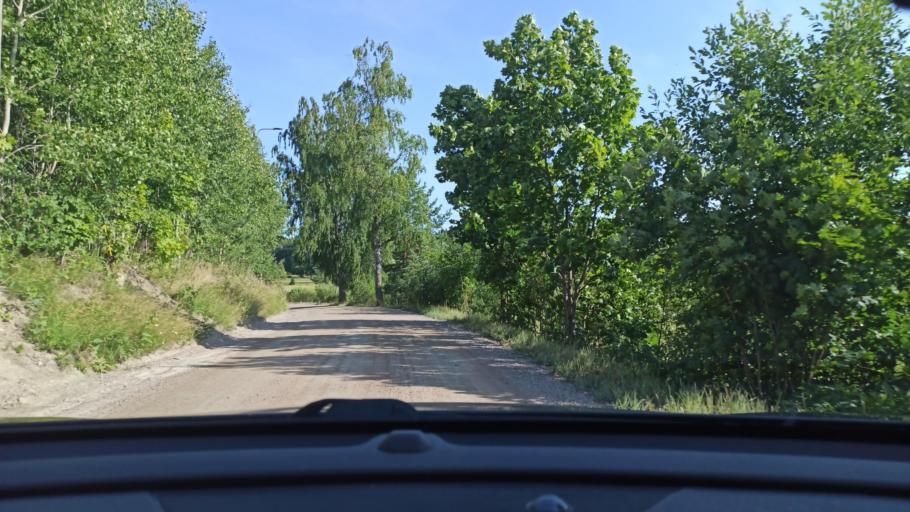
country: FI
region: Uusimaa
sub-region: Helsinki
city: Espoo
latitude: 60.2074
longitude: 24.5549
